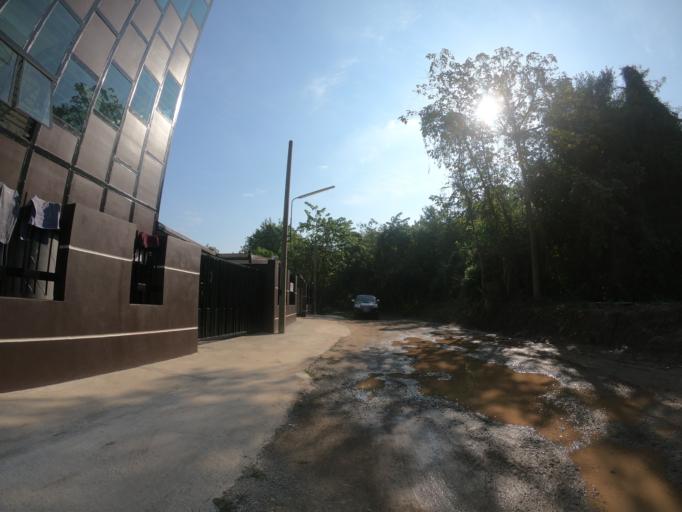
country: TH
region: Chiang Mai
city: Chiang Mai
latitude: 18.7484
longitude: 98.9832
